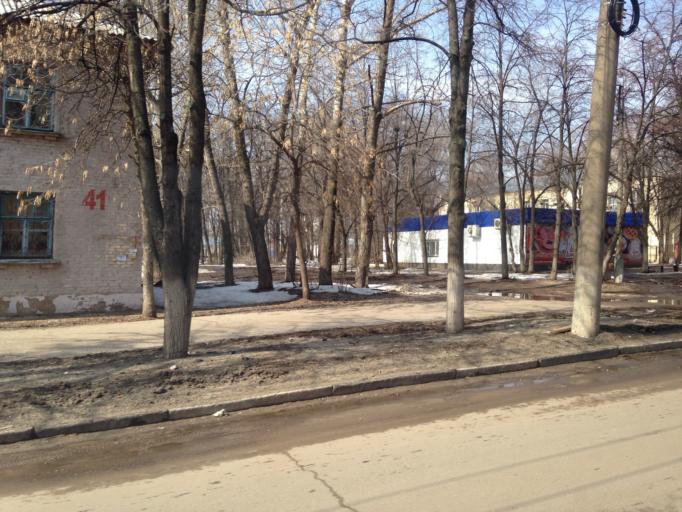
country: RU
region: Ulyanovsk
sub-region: Ulyanovskiy Rayon
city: Ulyanovsk
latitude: 54.3434
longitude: 48.5489
